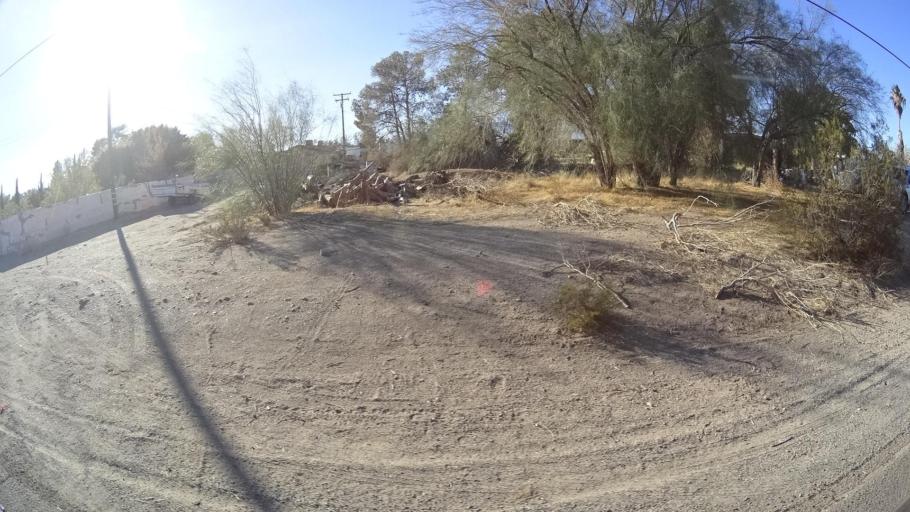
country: US
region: California
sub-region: Kern County
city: Ridgecrest
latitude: 35.6420
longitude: -117.7056
